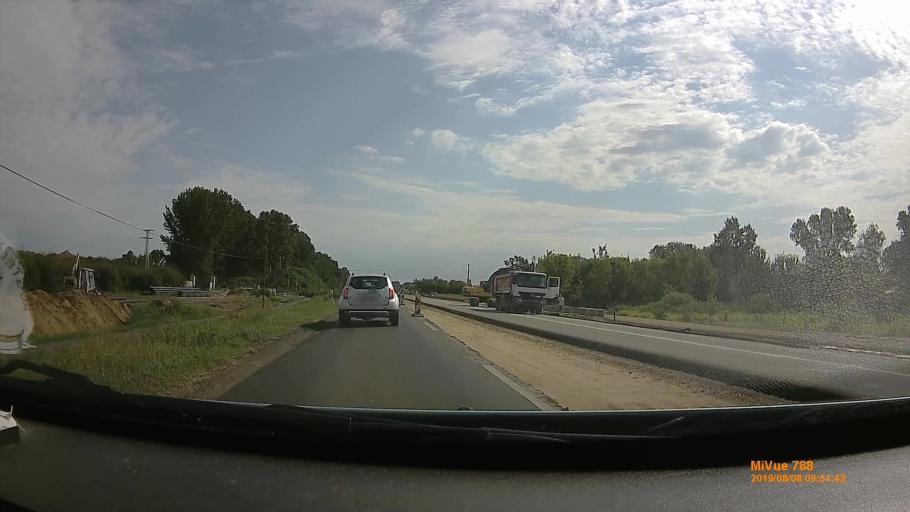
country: HU
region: Hajdu-Bihar
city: Debrecen
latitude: 47.5677
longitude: 21.6865
